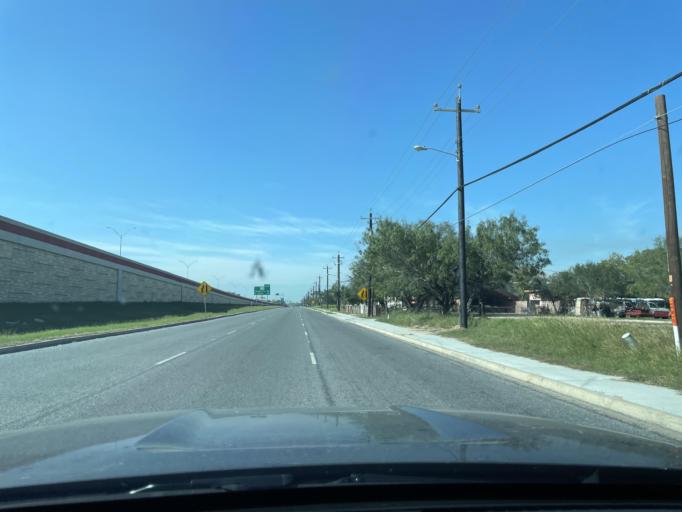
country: US
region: Texas
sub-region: Cameron County
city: Harlingen
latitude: 26.1652
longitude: -97.6886
